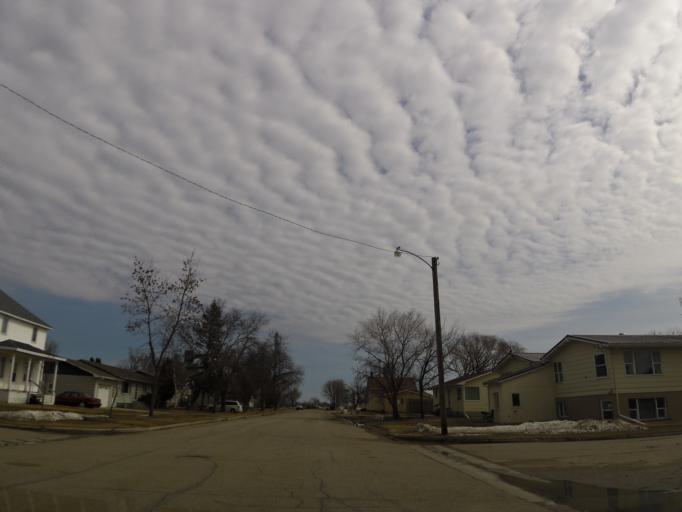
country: US
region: North Dakota
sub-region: Walsh County
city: Grafton
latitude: 48.2926
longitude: -97.3732
